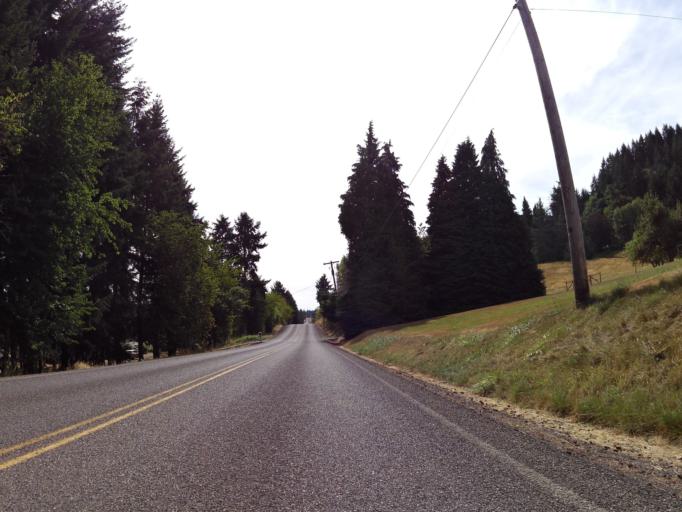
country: US
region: Washington
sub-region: Lewis County
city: Winlock
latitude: 46.5187
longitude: -122.9496
